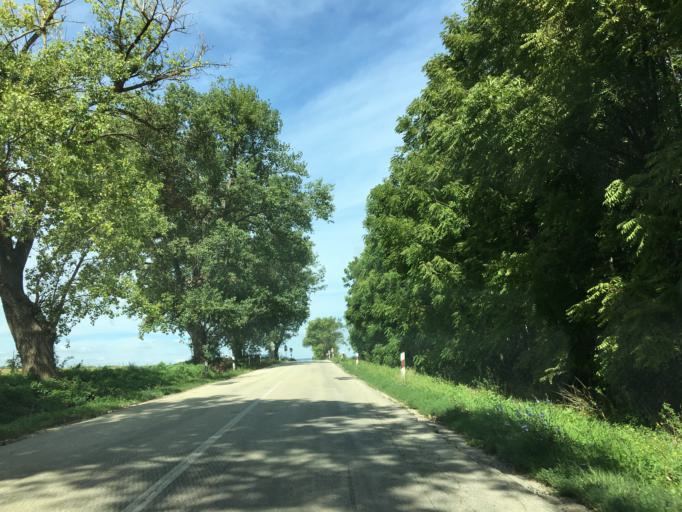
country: HU
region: Komarom-Esztergom
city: Bajna
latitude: 47.6120
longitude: 18.6399
